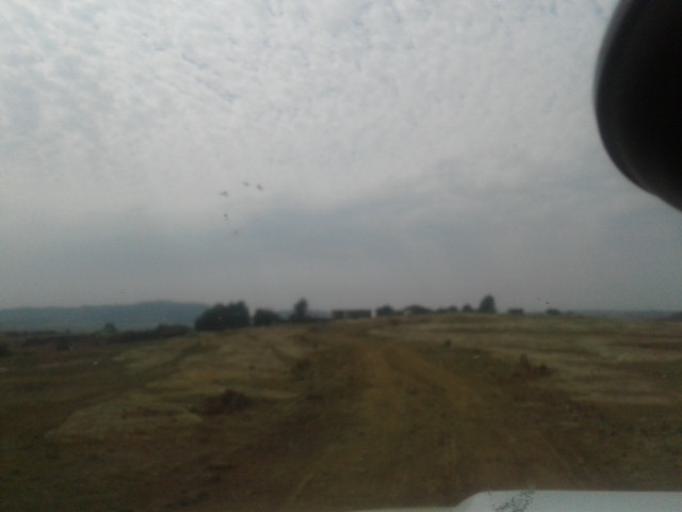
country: LS
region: Berea
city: Teyateyaneng
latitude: -29.1028
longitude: 27.9061
